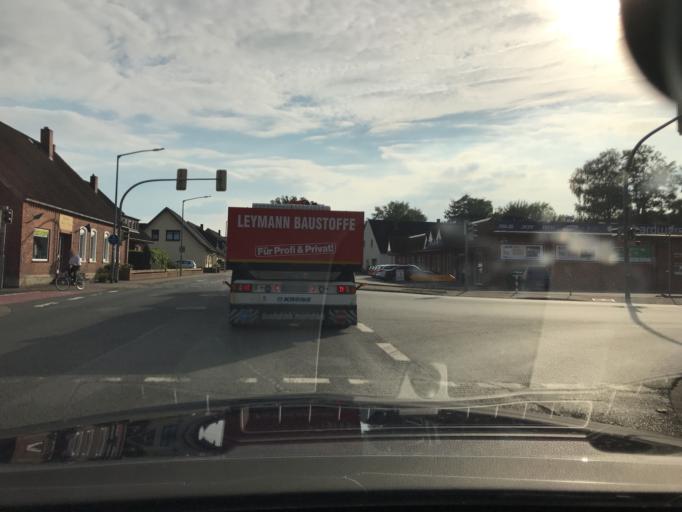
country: DE
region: Lower Saxony
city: Riede
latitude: 52.9849
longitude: 8.8792
